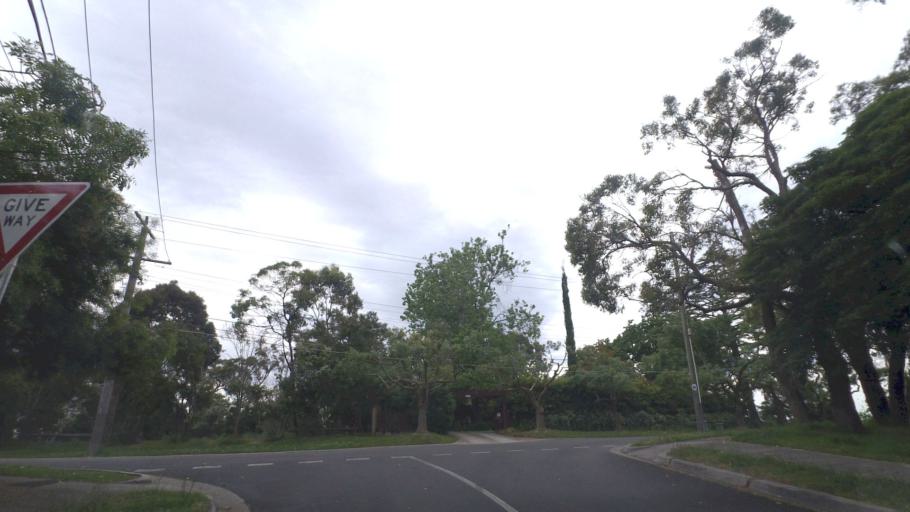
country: AU
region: Victoria
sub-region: Maroondah
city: Croydon Hills
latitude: -37.7917
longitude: 145.2715
